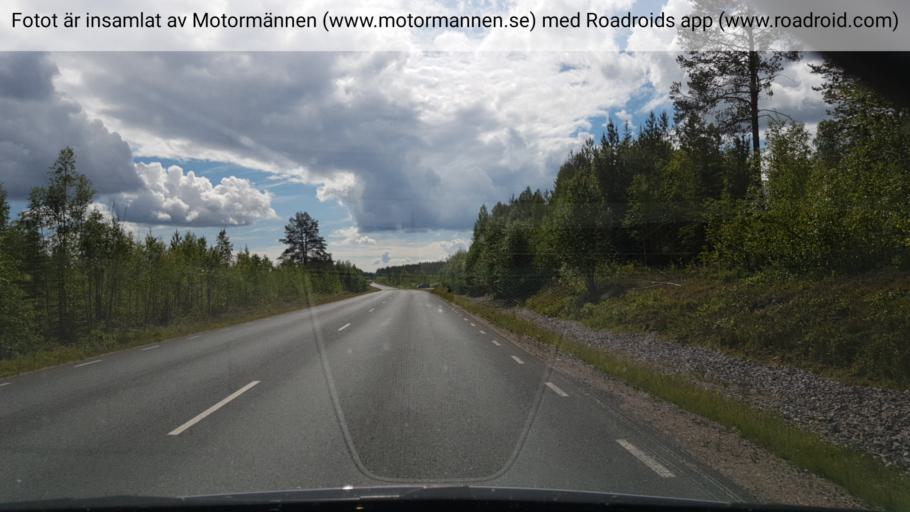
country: FI
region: Lapland
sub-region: Torniolaakso
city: Ylitornio
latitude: 66.3064
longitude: 23.6261
